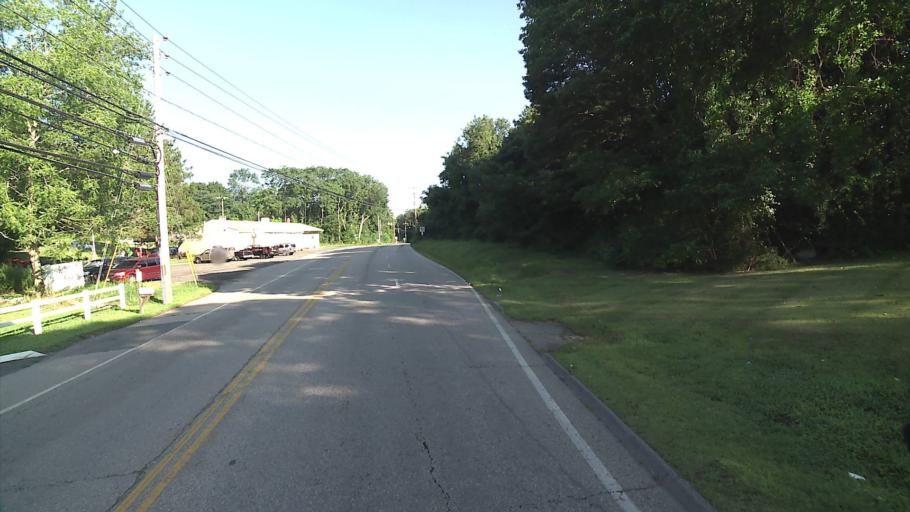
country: US
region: Connecticut
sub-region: New London County
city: Central Waterford
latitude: 41.3534
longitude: -72.1639
